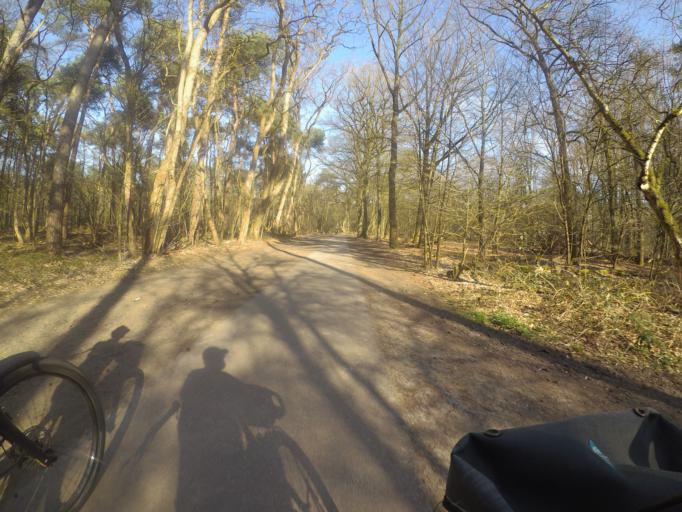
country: NL
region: North Brabant
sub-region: Gemeente Oisterwijk
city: Oisterwijk
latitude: 51.5615
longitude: 5.2050
